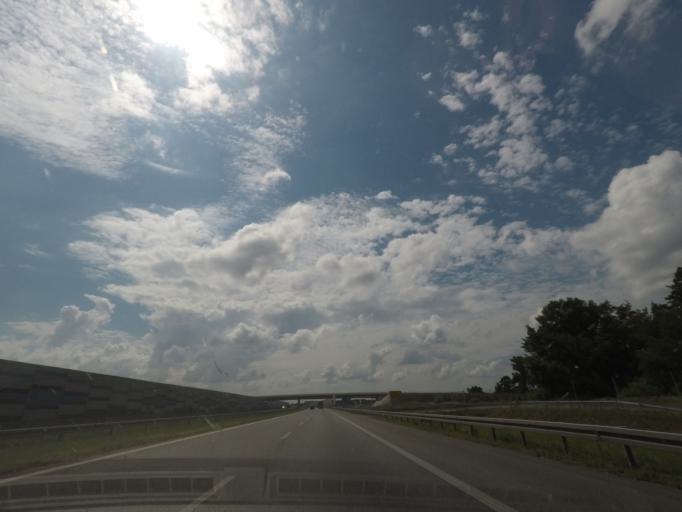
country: PL
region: Lodz Voivodeship
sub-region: Powiat leczycki
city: Piatek
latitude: 52.0199
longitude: 19.5418
